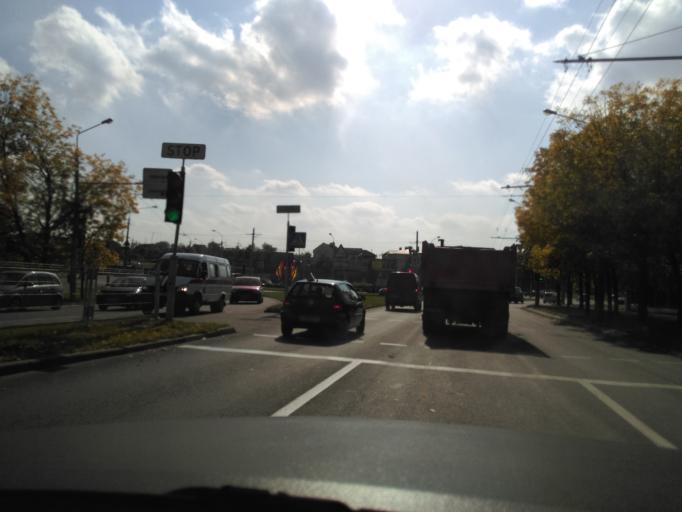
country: BY
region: Minsk
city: Minsk
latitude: 53.9081
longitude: 27.6312
